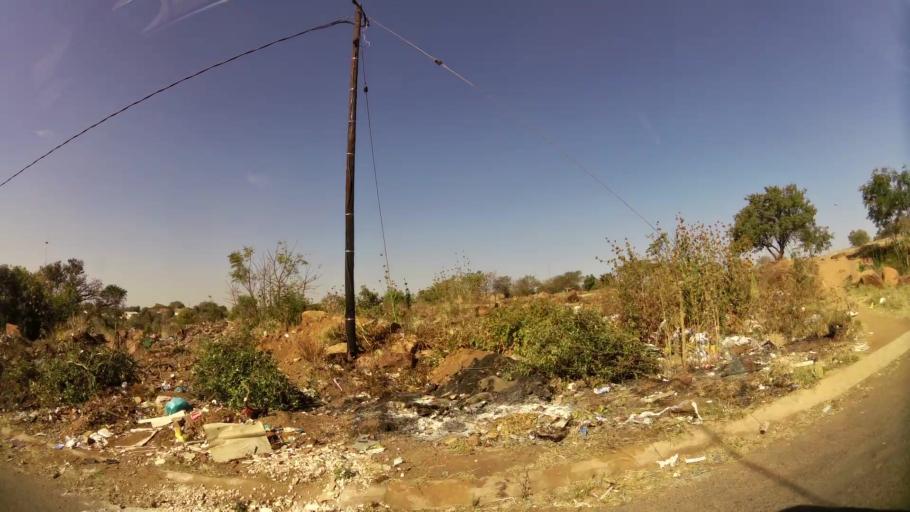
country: ZA
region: Gauteng
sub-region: City of Tshwane Metropolitan Municipality
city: Mabopane
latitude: -25.5334
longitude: 28.0958
